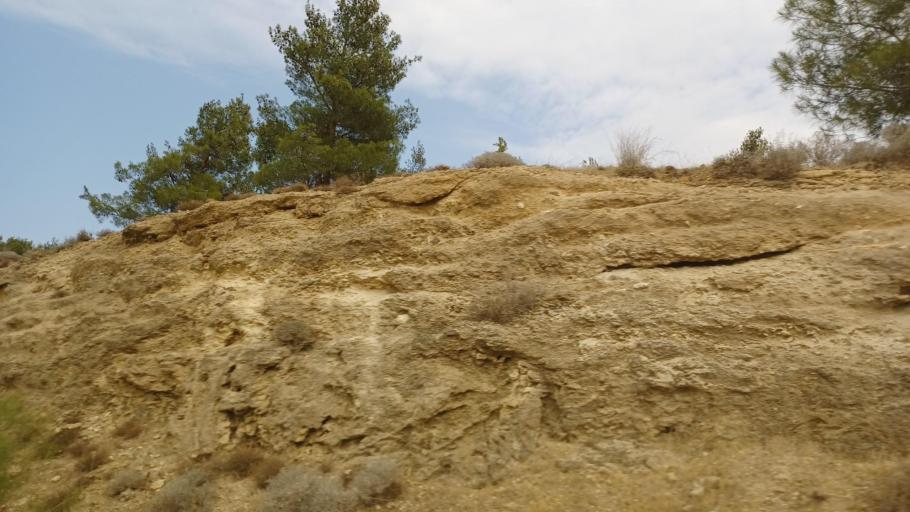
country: CY
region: Lefkosia
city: Klirou
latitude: 35.0409
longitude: 33.1095
